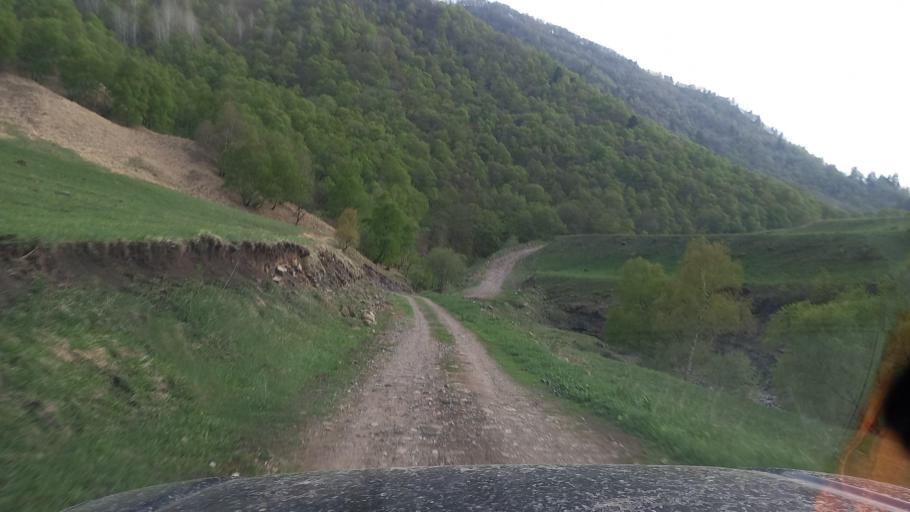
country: RU
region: Kabardino-Balkariya
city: Kamennomostskoye
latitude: 43.7172
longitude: 42.8415
